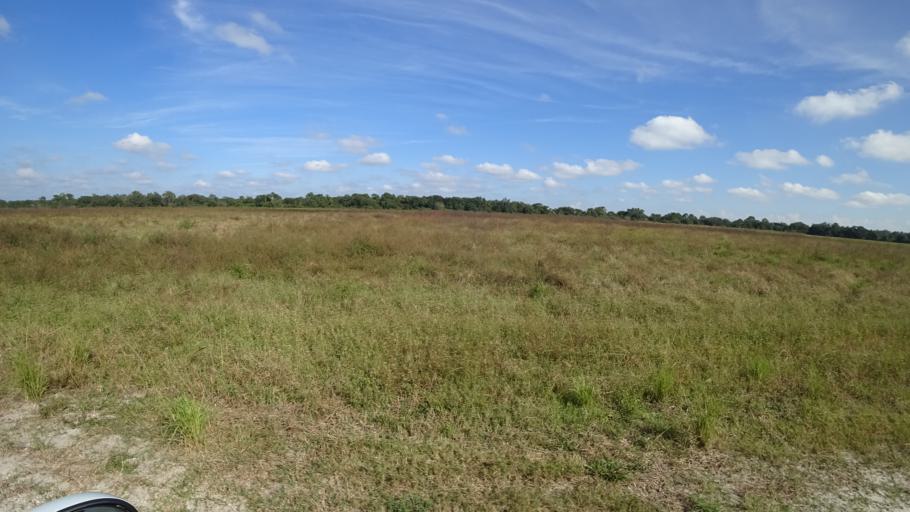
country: US
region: Florida
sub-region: Sarasota County
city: Lake Sarasota
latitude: 27.3646
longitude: -82.1574
